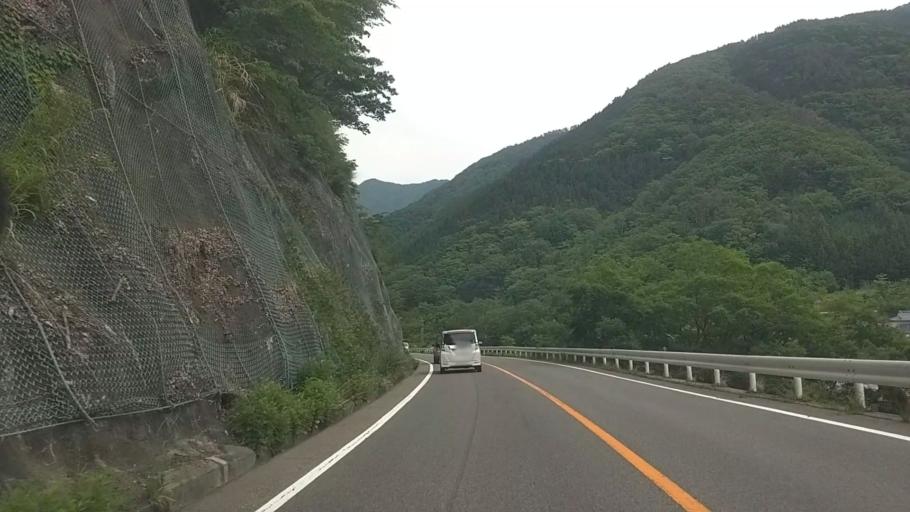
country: JP
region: Yamanashi
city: Fujikawaguchiko
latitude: 35.5365
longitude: 138.5939
